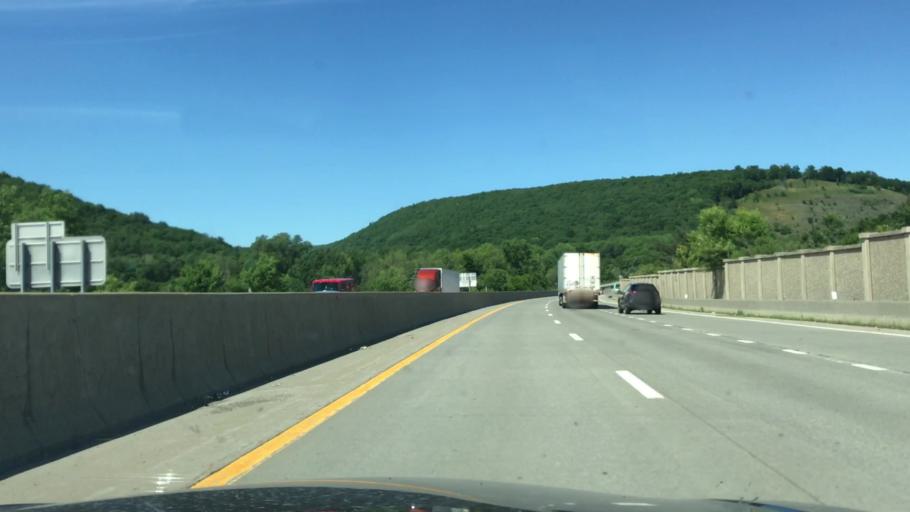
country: US
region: New York
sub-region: Steuben County
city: Painted Post
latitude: 42.1587
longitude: -77.0759
